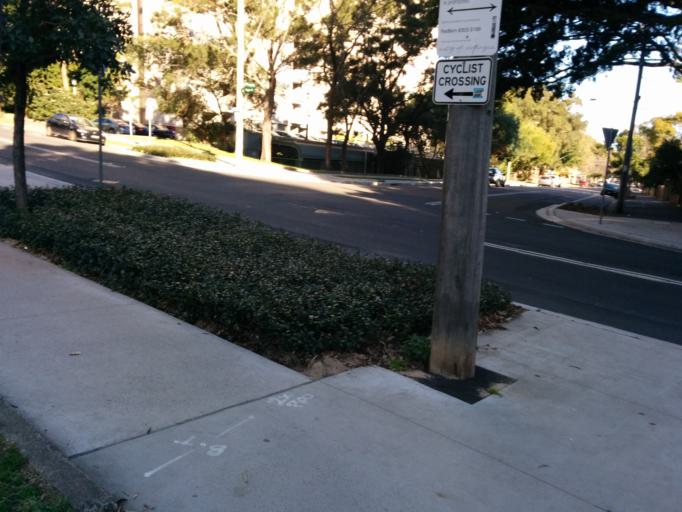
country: AU
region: New South Wales
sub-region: City of Sydney
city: Redfern
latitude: -33.8967
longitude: 151.2018
